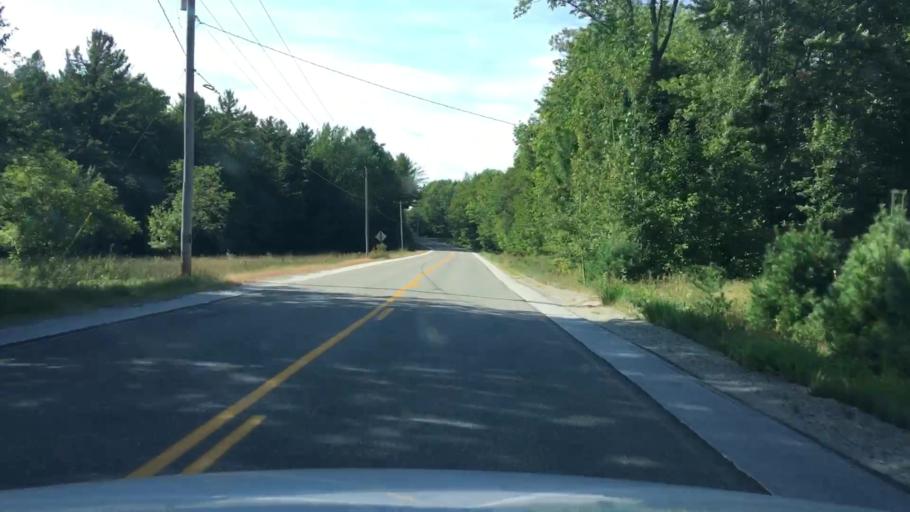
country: US
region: Maine
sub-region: Penobscot County
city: Enfield
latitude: 45.2143
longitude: -68.5272
